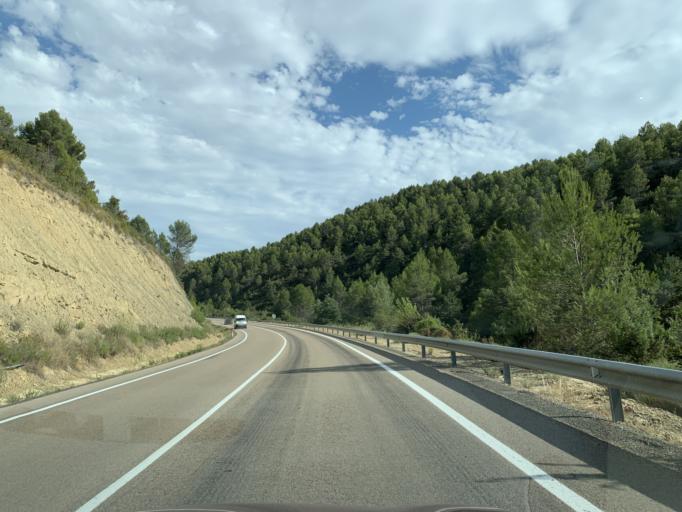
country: ES
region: Aragon
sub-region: Provincia de Zaragoza
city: Santa Eulalia de Gallego
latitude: 42.2970
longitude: -0.7321
